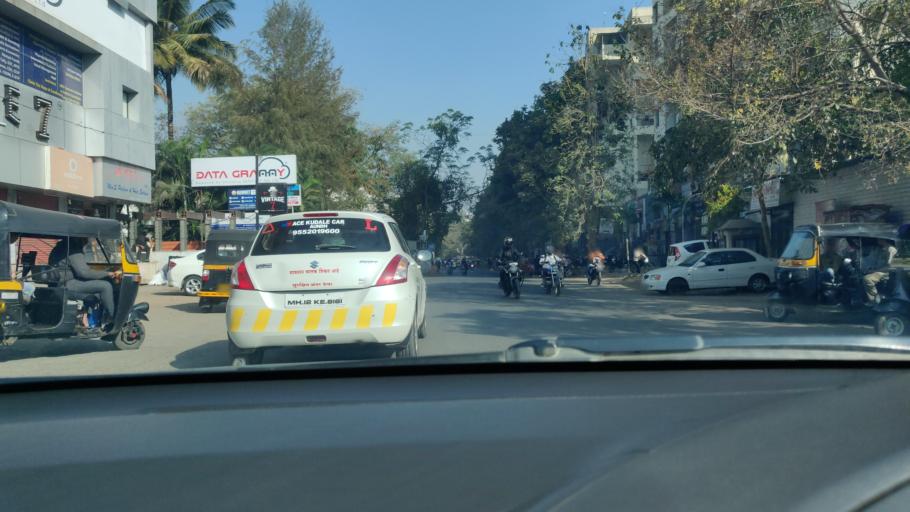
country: IN
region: Maharashtra
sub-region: Pune Division
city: Khadki
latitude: 18.5633
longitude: 73.8027
